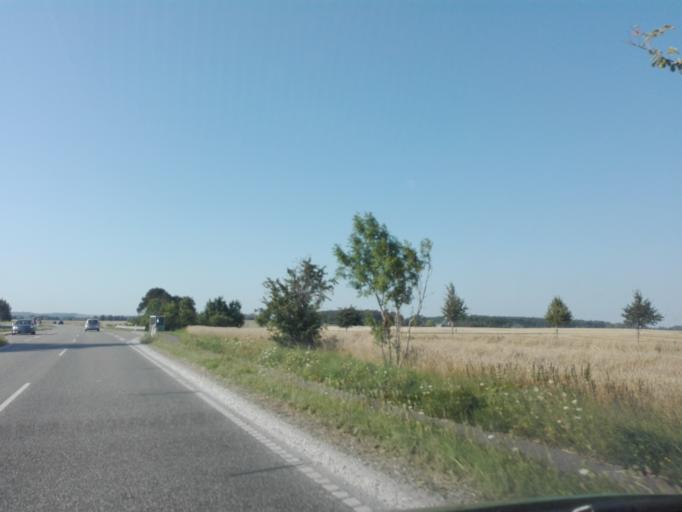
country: DK
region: Central Jutland
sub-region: Odder Kommune
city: Odder
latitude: 55.9478
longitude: 10.2045
